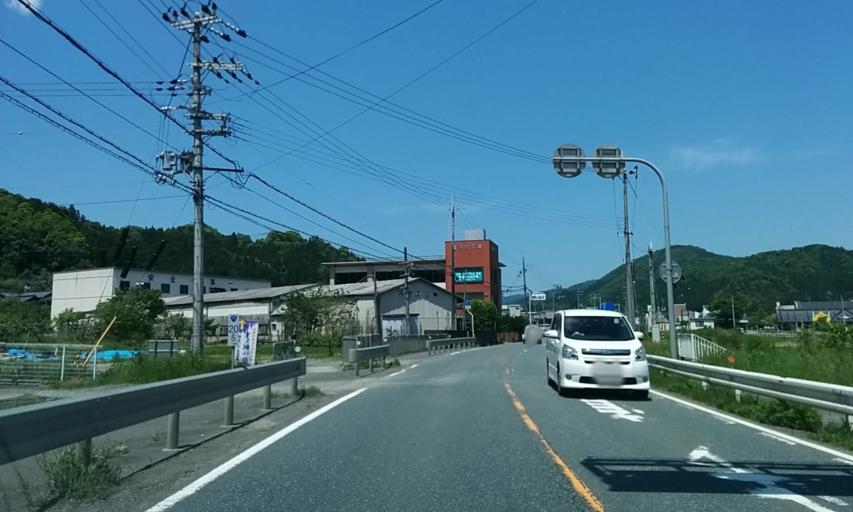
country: JP
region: Kyoto
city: Fukuchiyama
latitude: 35.3870
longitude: 135.1450
